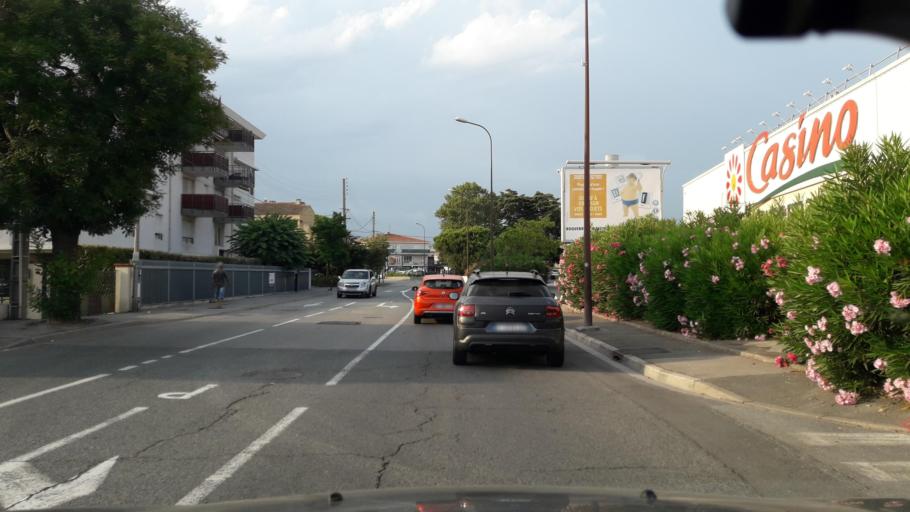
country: FR
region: Provence-Alpes-Cote d'Azur
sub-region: Departement du Var
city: Frejus
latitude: 43.4314
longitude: 6.7543
